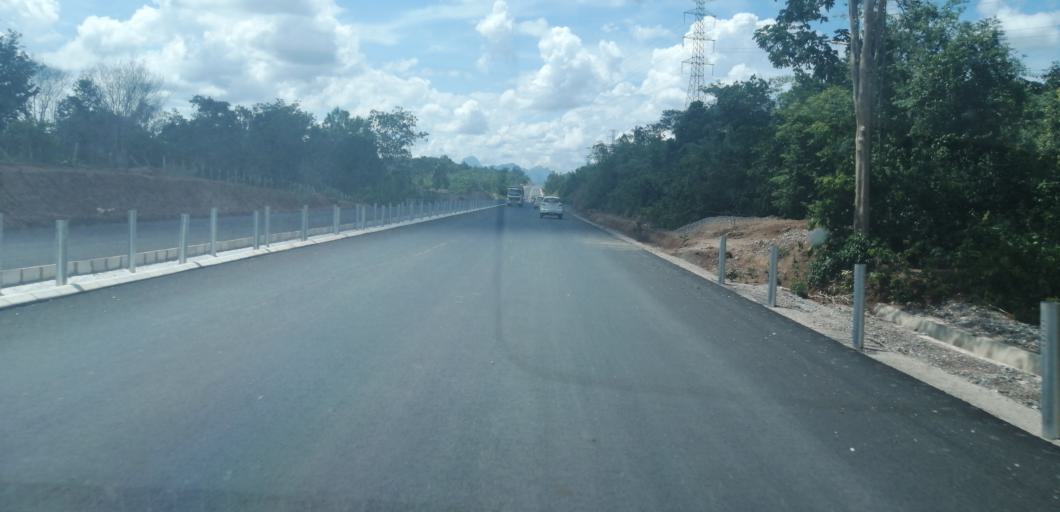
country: LA
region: Vientiane
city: Muang Phon-Hong
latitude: 18.6088
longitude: 102.3244
